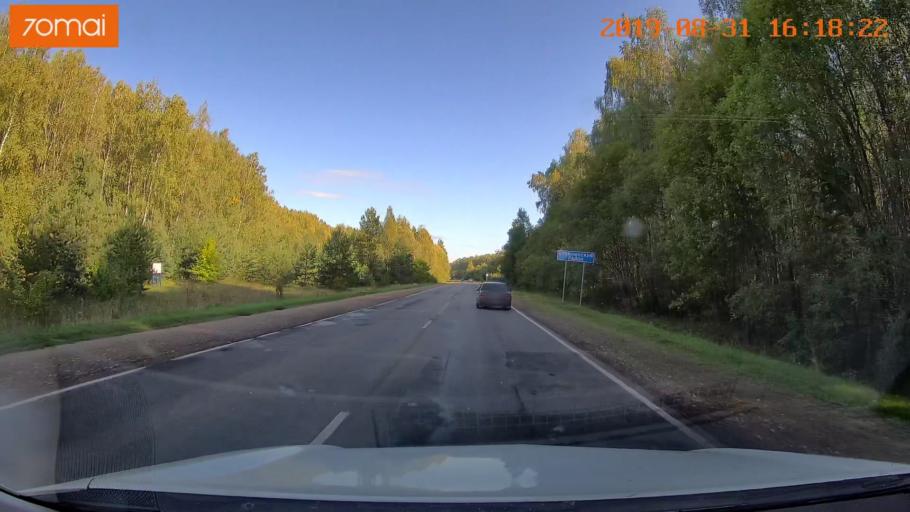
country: RU
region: Kaluga
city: Nikola-Lenivets
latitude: 54.5370
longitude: 35.5536
